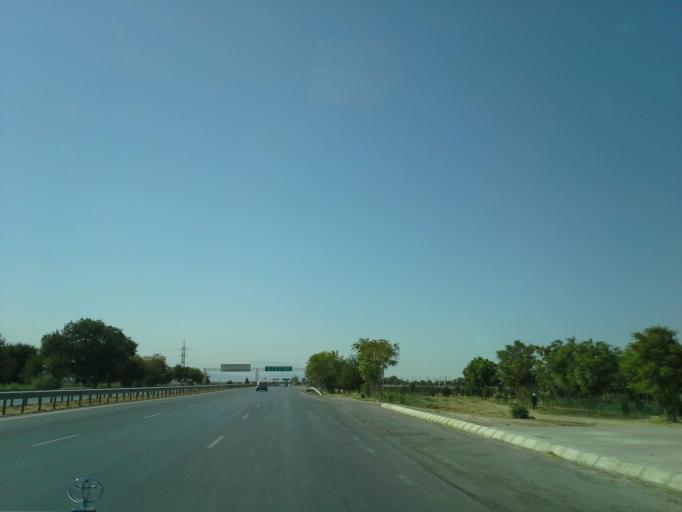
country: TM
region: Ahal
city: Annau
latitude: 37.9035
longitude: 58.5529
